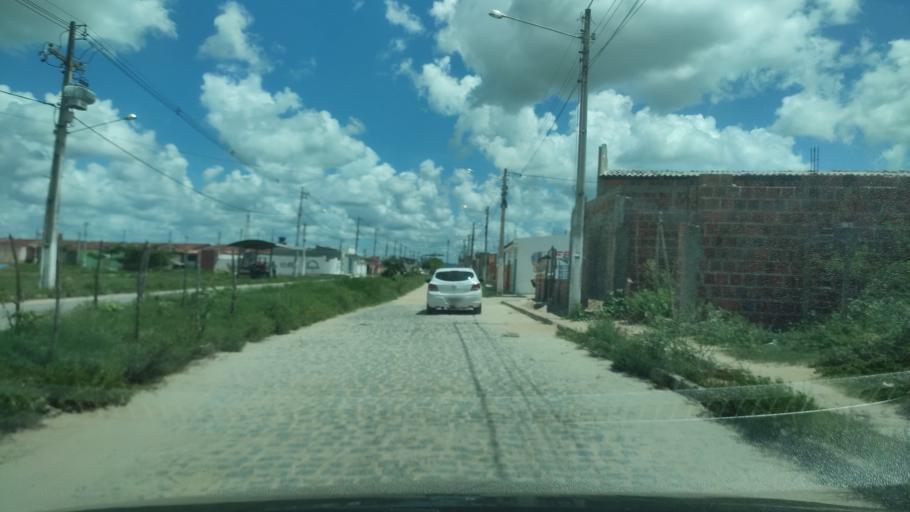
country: BR
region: Alagoas
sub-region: Uniao Dos Palmares
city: Uniao dos Palmares
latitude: -9.1475
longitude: -36.0039
